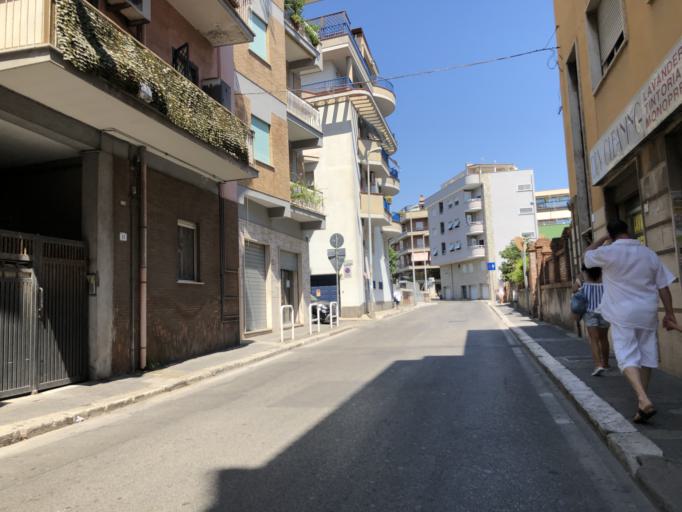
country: IT
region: Latium
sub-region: Citta metropolitana di Roma Capitale
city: Nettuno
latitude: 41.4588
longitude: 12.6557
